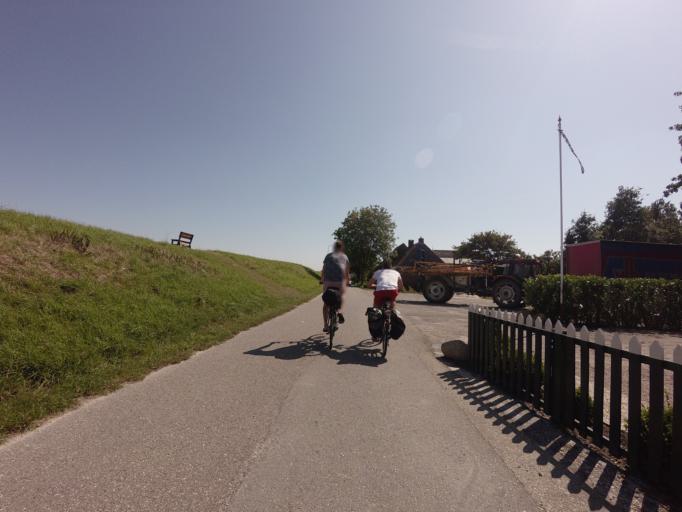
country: NL
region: Friesland
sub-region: Gemeente Dongeradeel
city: Anjum
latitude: 53.3959
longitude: 6.1077
